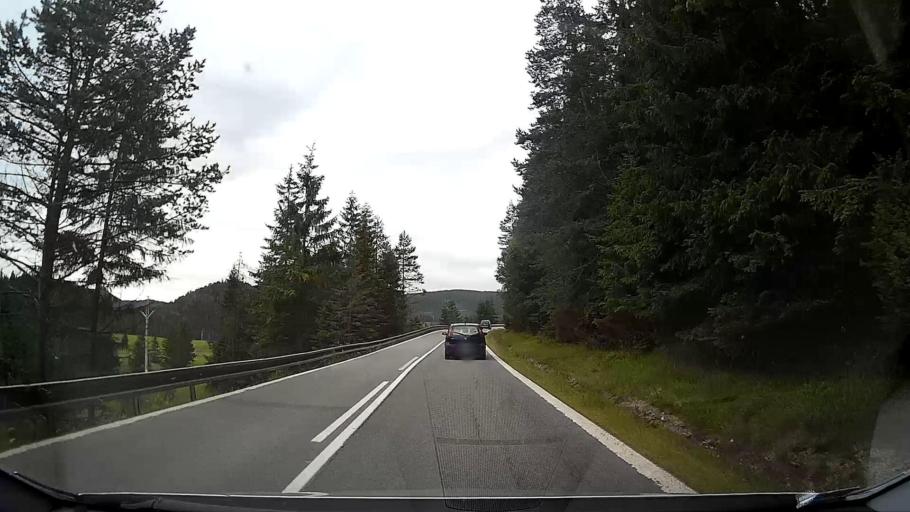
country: SK
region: Kosicky
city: Dobsina
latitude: 48.8744
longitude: 20.2301
